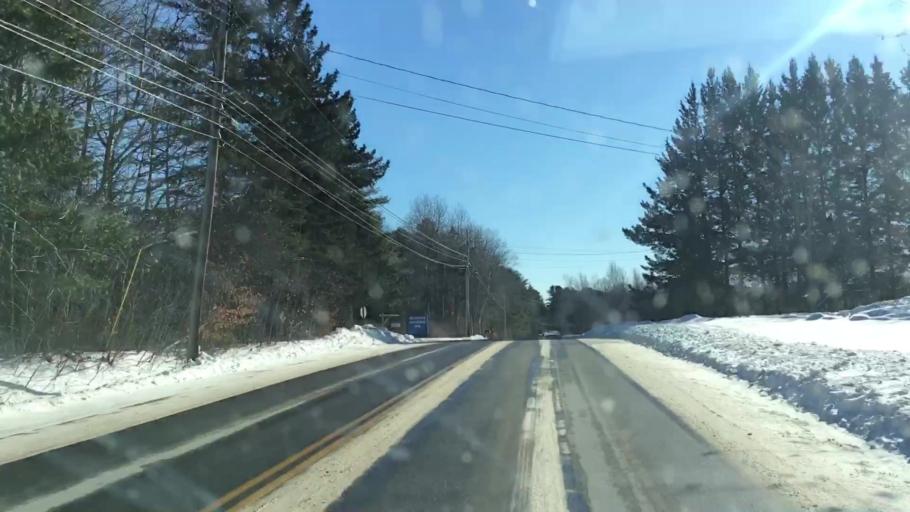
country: US
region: Maine
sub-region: Sagadahoc County
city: Topsham
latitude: 43.9061
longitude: -70.0043
